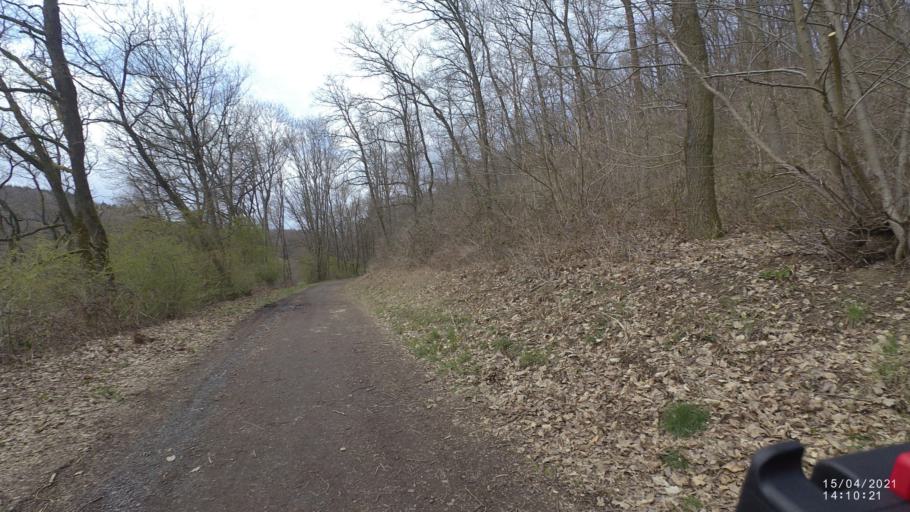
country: DE
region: Rheinland-Pfalz
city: Bell
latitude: 50.3790
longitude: 7.2328
